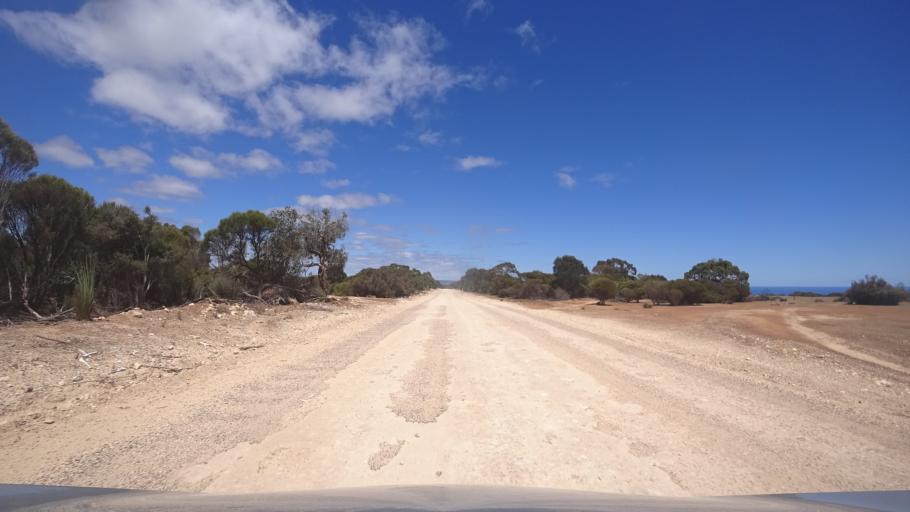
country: AU
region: South Australia
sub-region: Kangaroo Island
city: Kingscote
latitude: -35.6372
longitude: 137.2421
